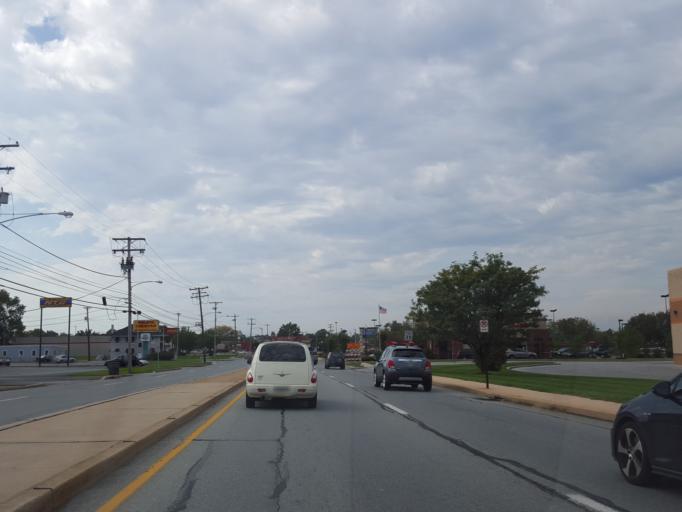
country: US
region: Pennsylvania
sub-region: York County
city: East York
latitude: 39.9764
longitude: -76.6687
